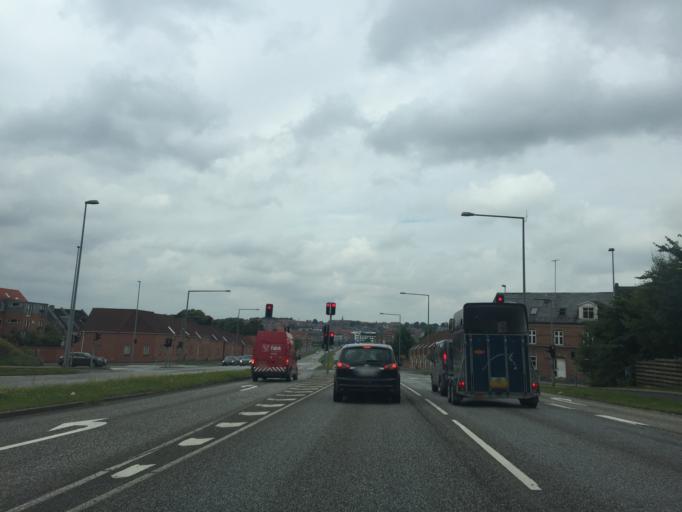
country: DK
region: Central Jutland
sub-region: Randers Kommune
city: Randers
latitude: 56.4507
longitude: 10.0451
